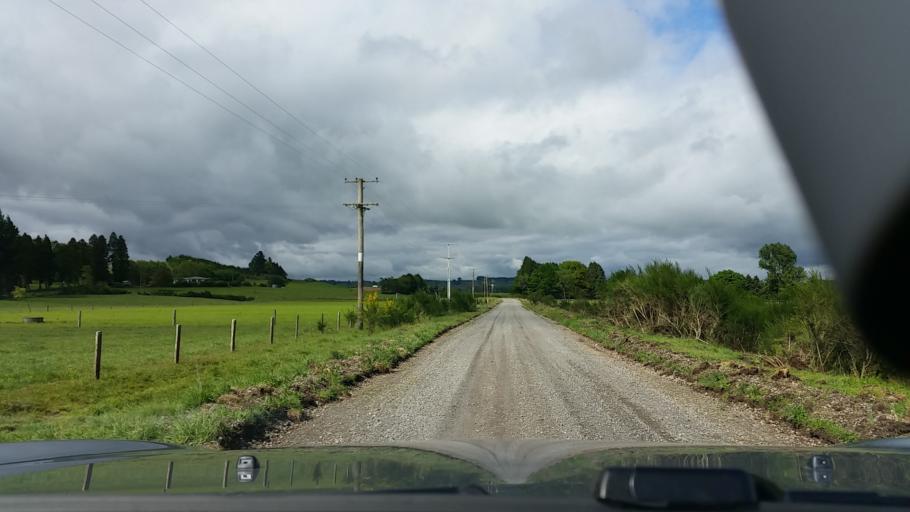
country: NZ
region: Bay of Plenty
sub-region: Whakatane District
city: Murupara
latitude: -38.2892
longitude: 176.5469
